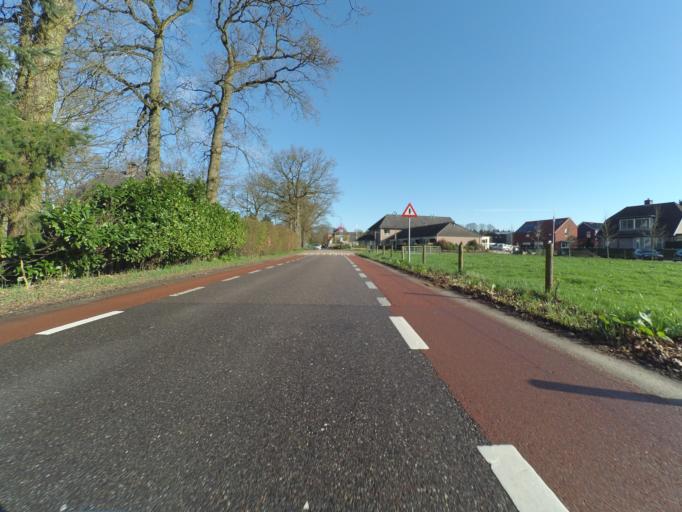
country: NL
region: Gelderland
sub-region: Gemeente Apeldoorn
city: Beekbergen
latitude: 52.1150
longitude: 5.8751
